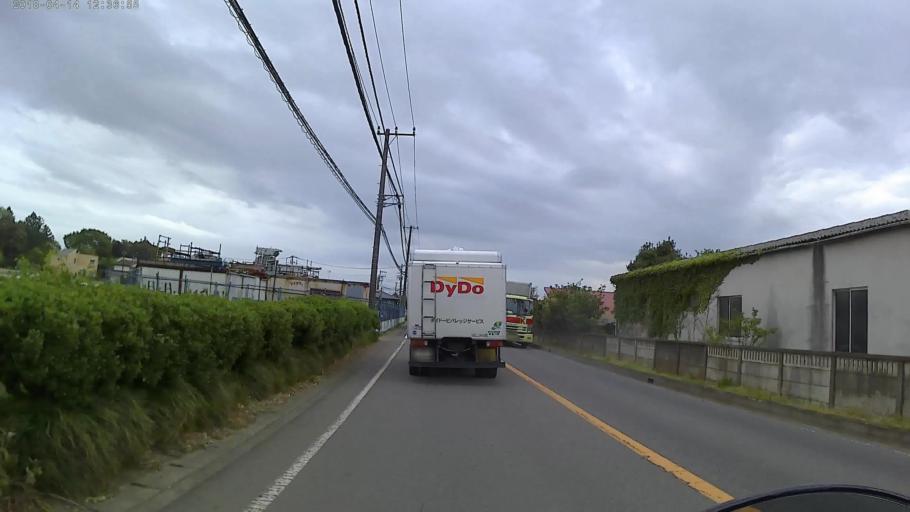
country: JP
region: Kanagawa
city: Atsugi
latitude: 35.4138
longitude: 139.4068
